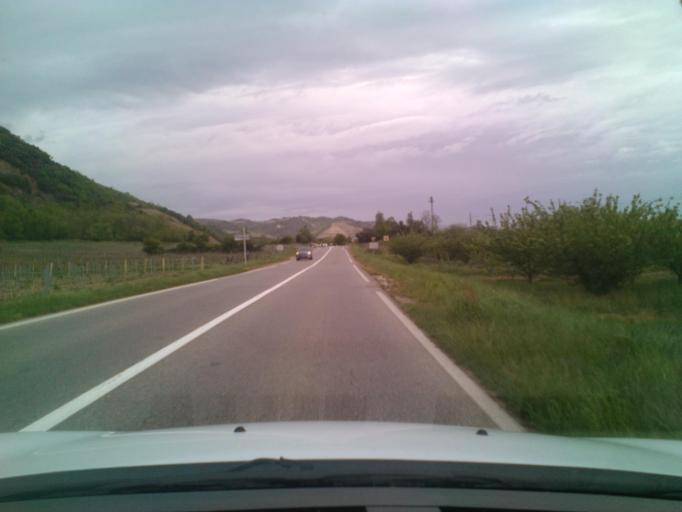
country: FR
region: Rhone-Alpes
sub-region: Departement de l'Ardeche
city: Mauves
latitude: 45.0218
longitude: 4.8322
